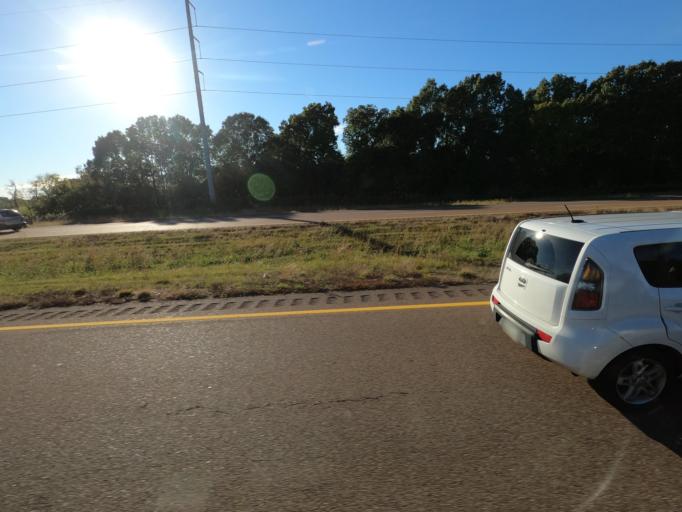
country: US
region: Tennessee
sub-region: Fayette County
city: Piperton
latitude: 35.0506
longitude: -89.6376
